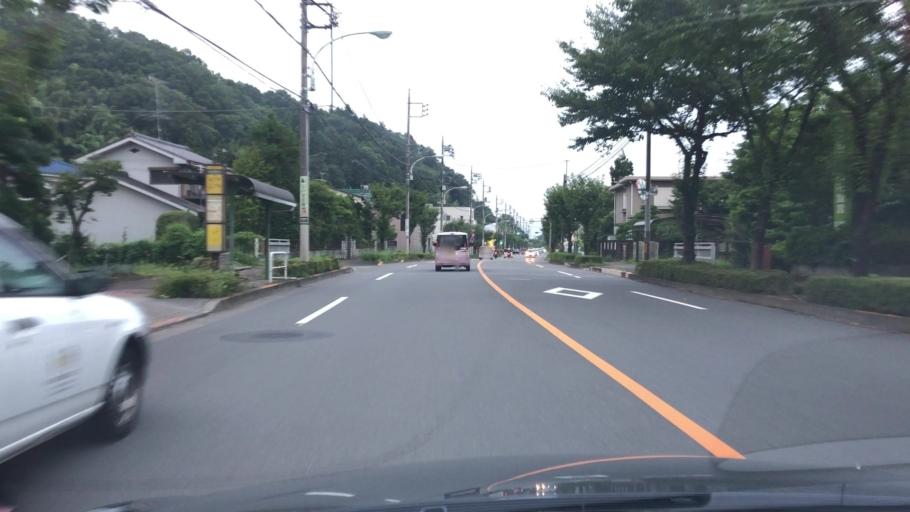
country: JP
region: Tokyo
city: Itsukaichi
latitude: 35.7426
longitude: 139.2579
